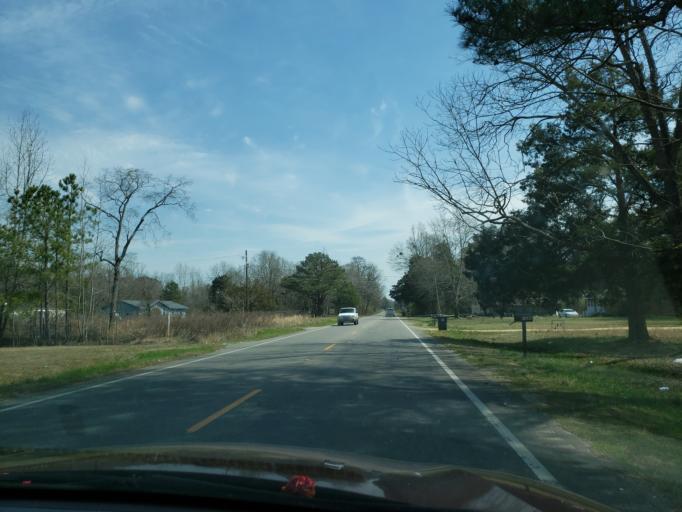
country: US
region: Alabama
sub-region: Autauga County
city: Prattville
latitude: 32.4309
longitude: -86.4992
